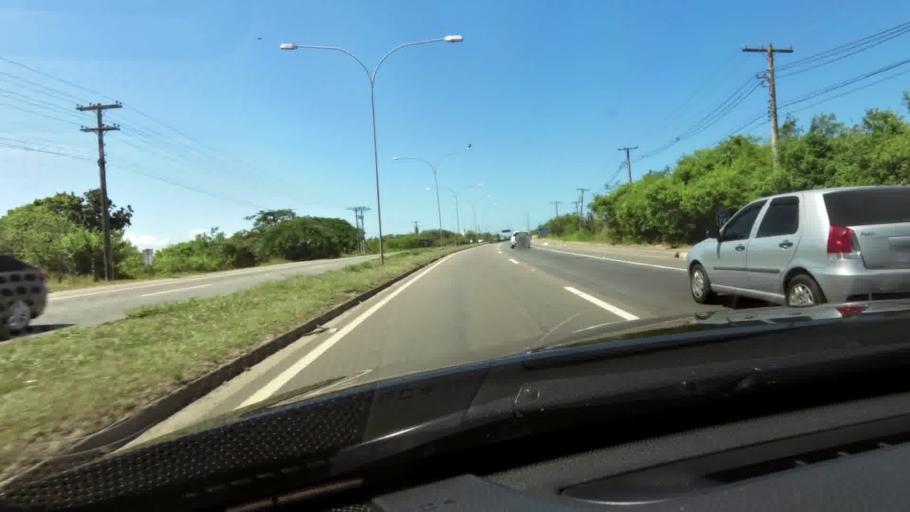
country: BR
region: Espirito Santo
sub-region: Vila Velha
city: Vila Velha
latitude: -20.4021
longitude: -40.3250
